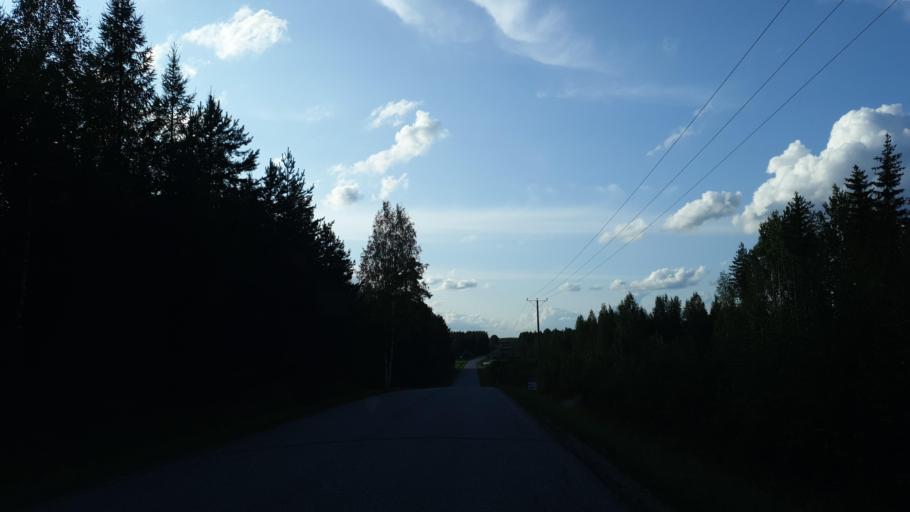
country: FI
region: Northern Savo
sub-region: Koillis-Savo
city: Kaavi
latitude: 62.9819
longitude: 28.7422
